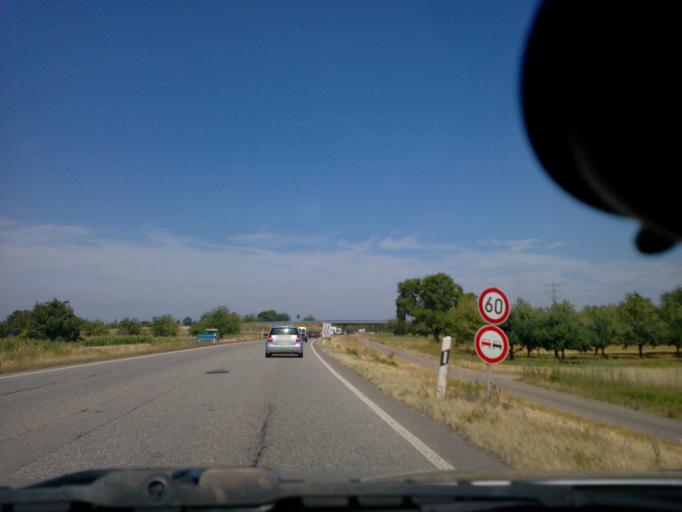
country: DE
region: Baden-Wuerttemberg
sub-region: Freiburg Region
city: Ortenberg
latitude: 48.4332
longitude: 7.9616
